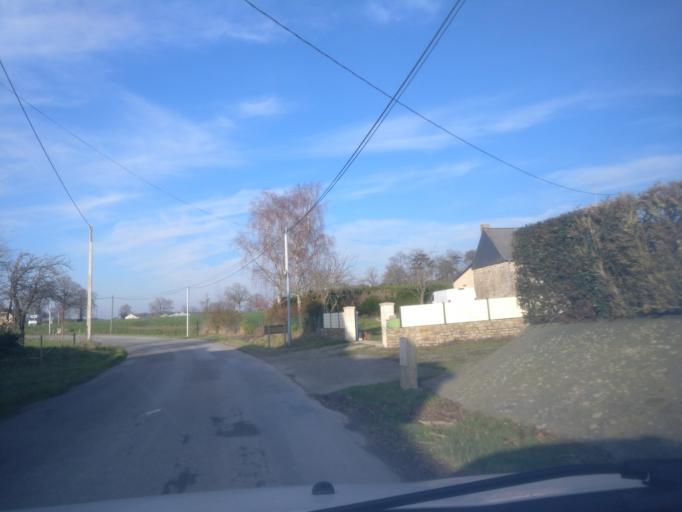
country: FR
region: Brittany
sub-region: Departement d'Ille-et-Vilaine
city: Livre-sur-Changeon
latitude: 48.1878
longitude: -1.3048
